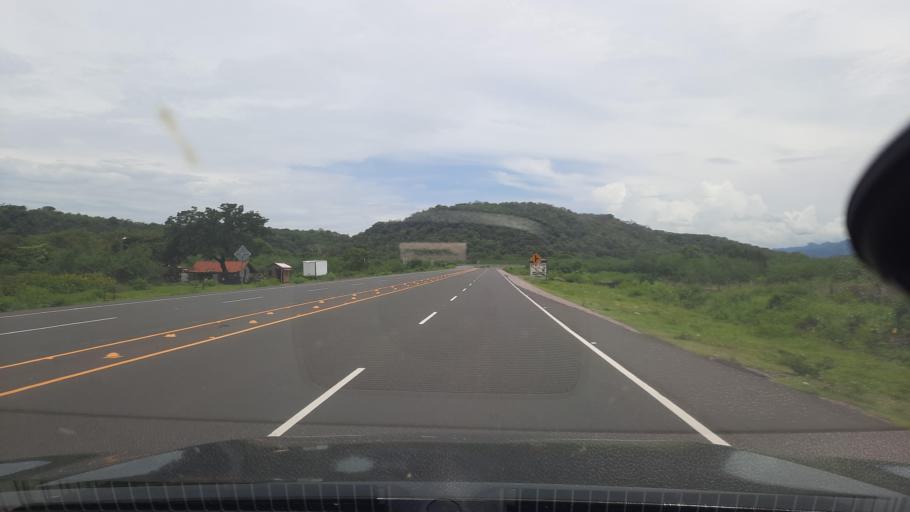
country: HN
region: Valle
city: Aramecina
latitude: 13.7277
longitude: -87.7117
